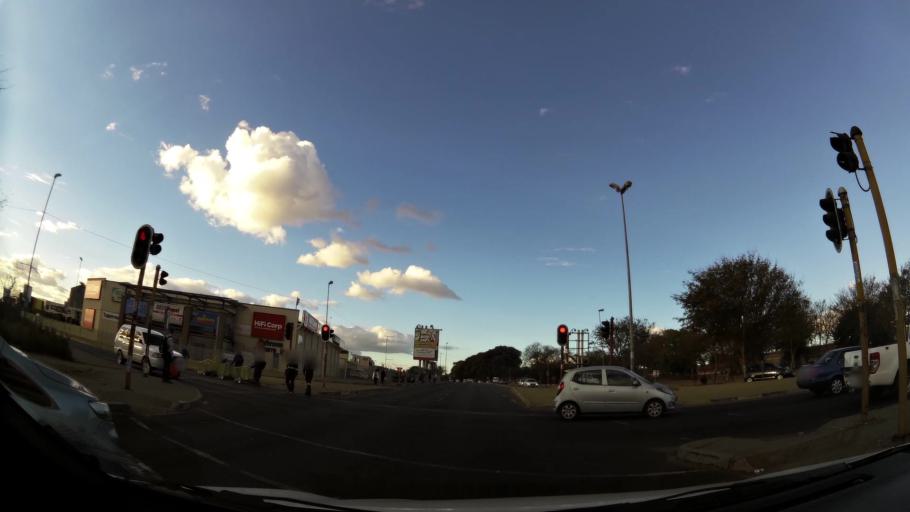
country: ZA
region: Limpopo
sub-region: Capricorn District Municipality
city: Polokwane
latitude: -23.8969
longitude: 29.4495
